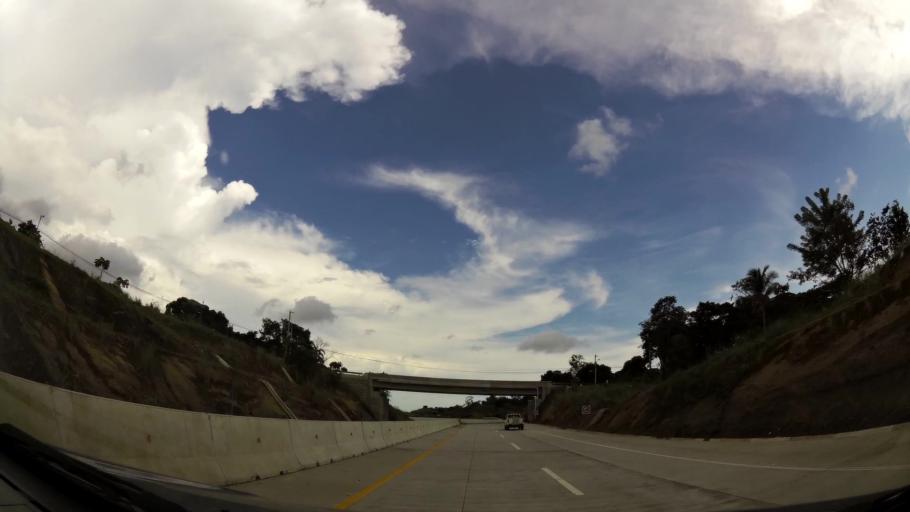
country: PA
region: Panama
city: Tocumen
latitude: 9.1065
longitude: -79.4003
